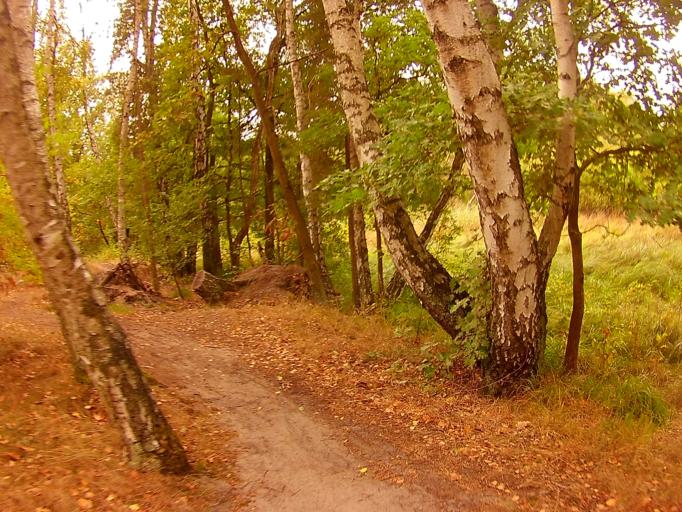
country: DE
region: Berlin
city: Grunau
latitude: 52.4057
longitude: 13.6052
